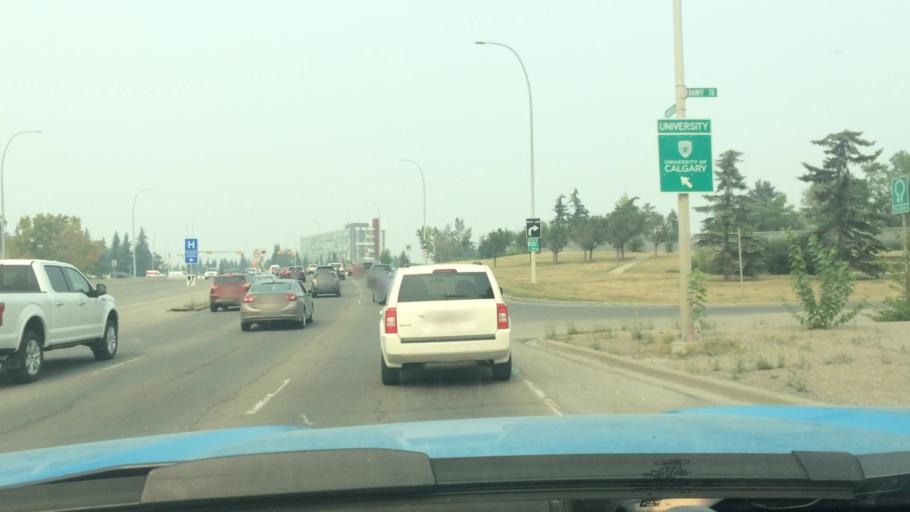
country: CA
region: Alberta
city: Calgary
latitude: 51.0723
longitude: -114.1179
